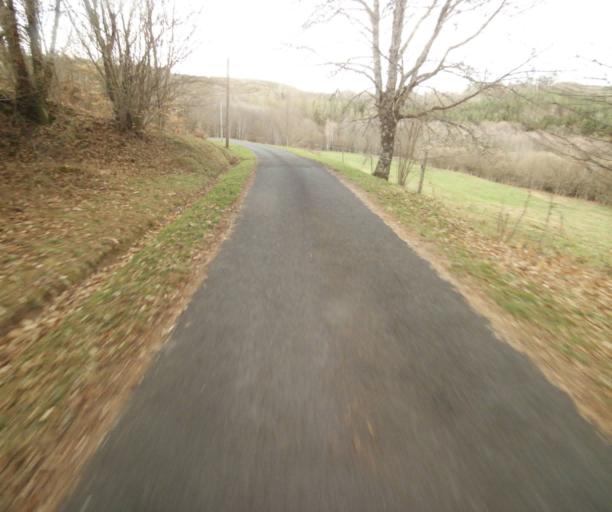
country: FR
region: Limousin
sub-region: Departement de la Correze
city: Egletons
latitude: 45.2659
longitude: 1.9943
